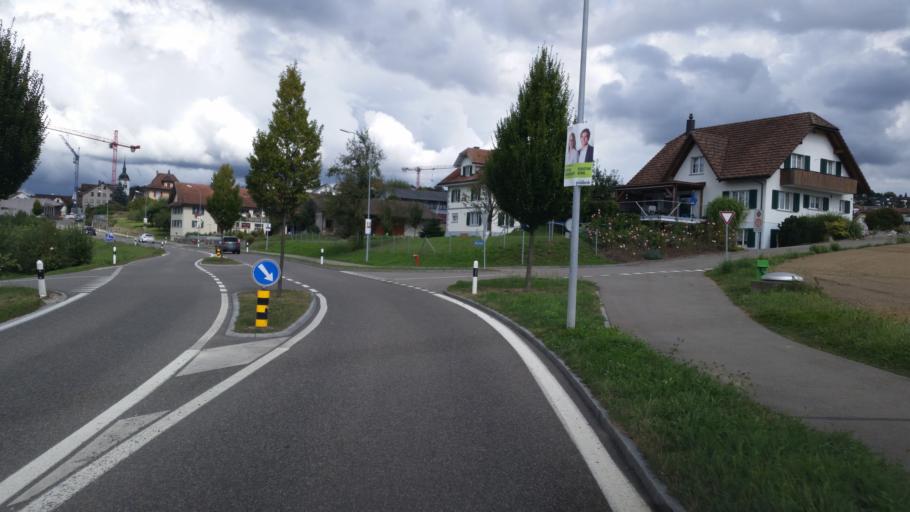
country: CH
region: Aargau
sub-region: Bezirk Bremgarten
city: Oberlunkhofen
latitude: 47.3075
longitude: 8.3905
